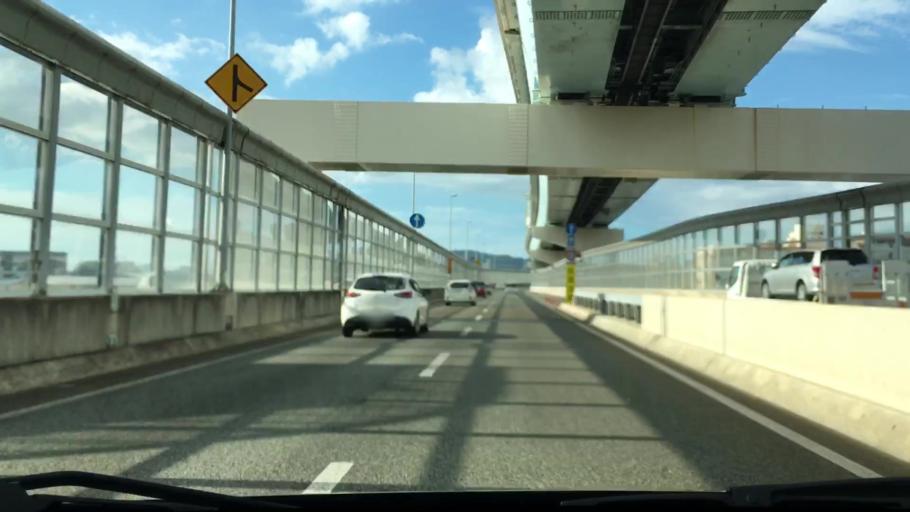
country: JP
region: Fukuoka
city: Fukuoka-shi
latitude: 33.5742
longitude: 130.3162
